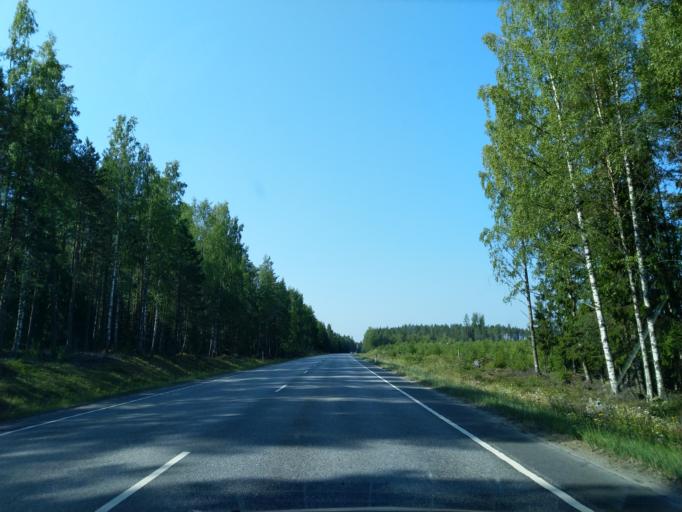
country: FI
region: Satakunta
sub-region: Pori
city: Noormarkku
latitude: 61.6367
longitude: 21.9402
